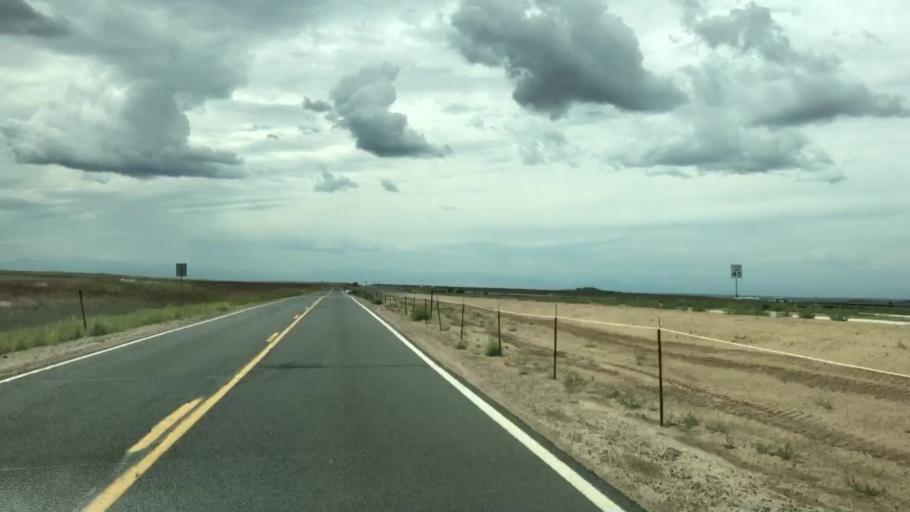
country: US
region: Colorado
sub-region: Adams County
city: Aurora
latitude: 39.7981
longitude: -104.6732
